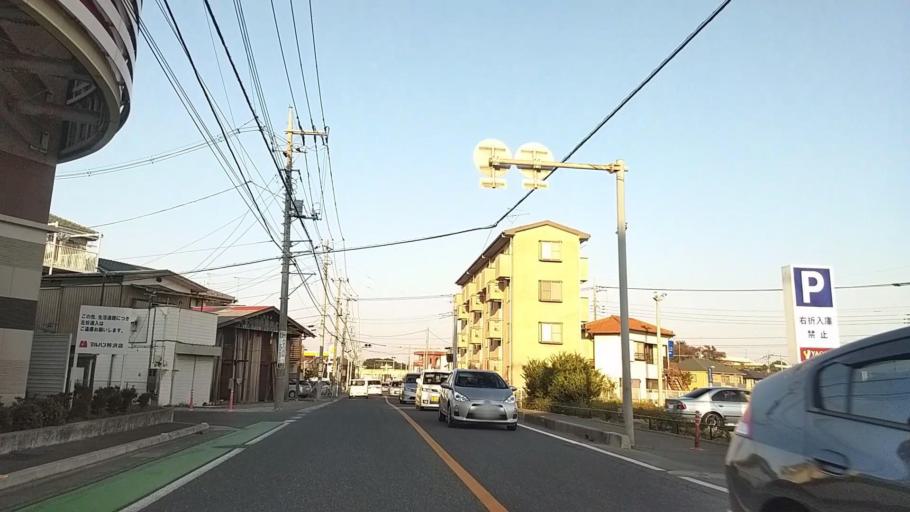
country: JP
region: Saitama
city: Tokorozawa
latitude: 35.8158
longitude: 139.4617
